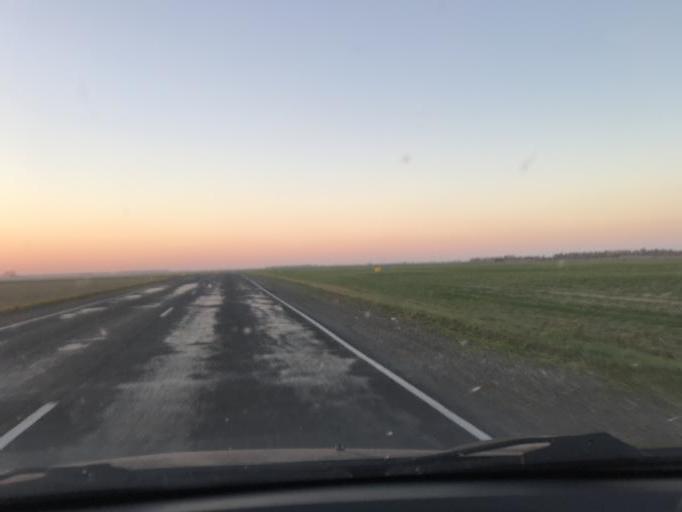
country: BY
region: Gomel
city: Horad Rechytsa
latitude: 52.1638
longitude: 30.5835
